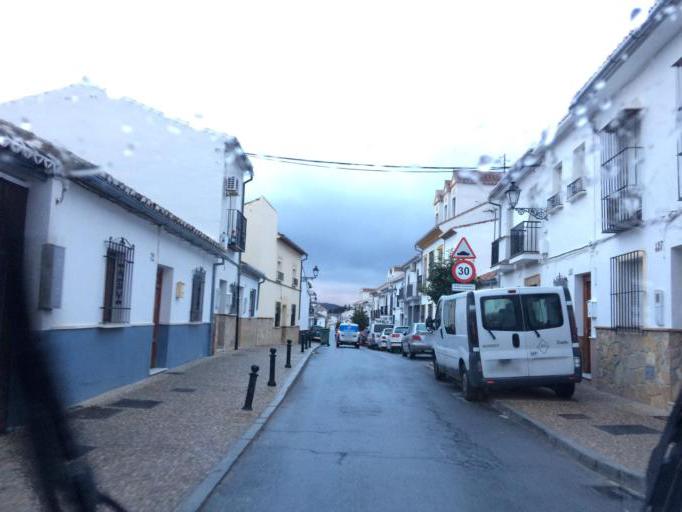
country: ES
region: Andalusia
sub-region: Provincia de Malaga
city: Antequera
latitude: 37.0216
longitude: -4.5538
